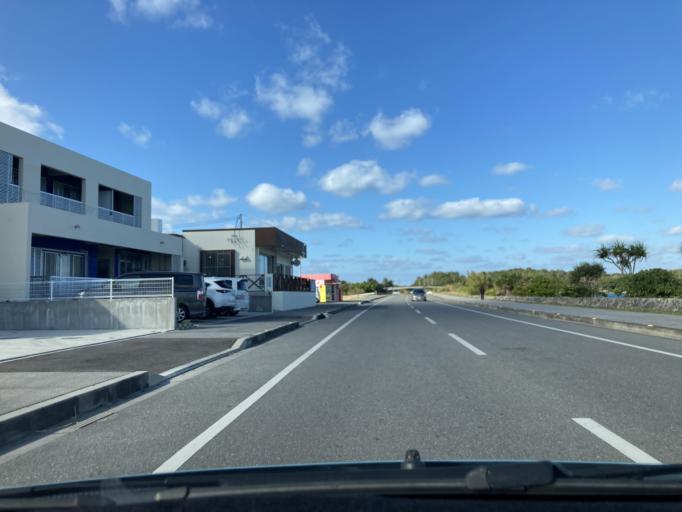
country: JP
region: Okinawa
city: Katsuren-haebaru
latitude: 26.3124
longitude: 127.9193
